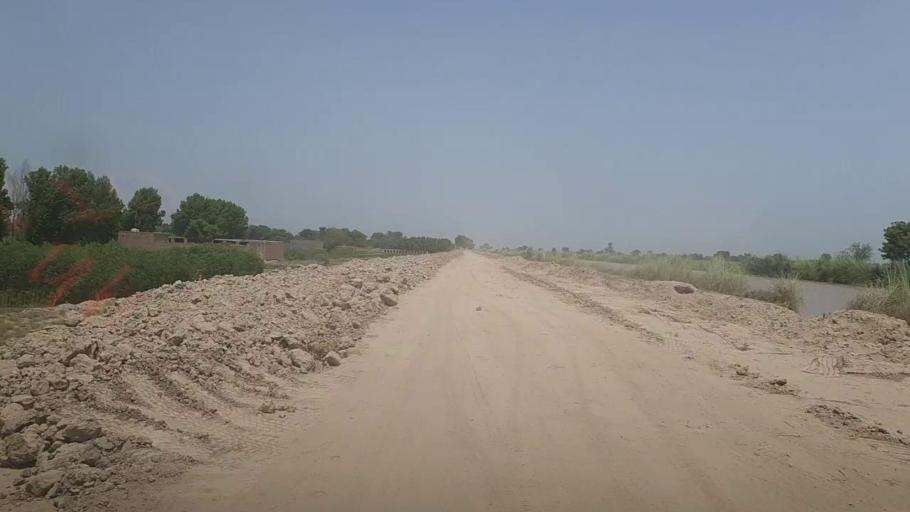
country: PK
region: Sindh
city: Pad Idan
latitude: 26.7874
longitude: 68.2770
